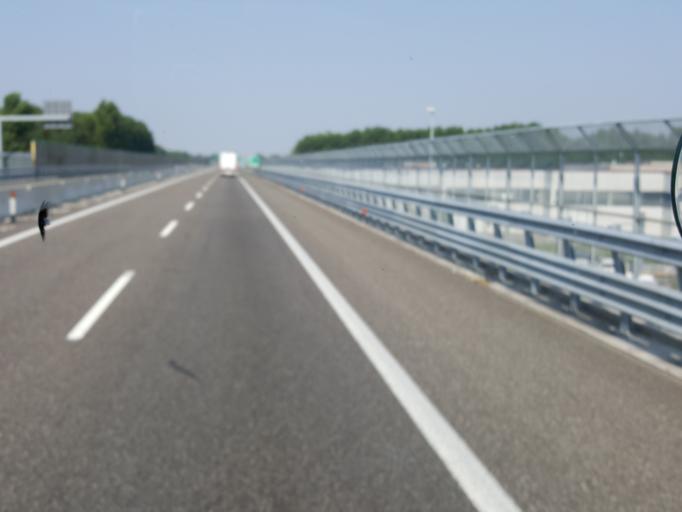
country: IT
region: Lombardy
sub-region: Provincia di Brescia
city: Capriano del Colle
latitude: 45.4796
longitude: 10.1424
